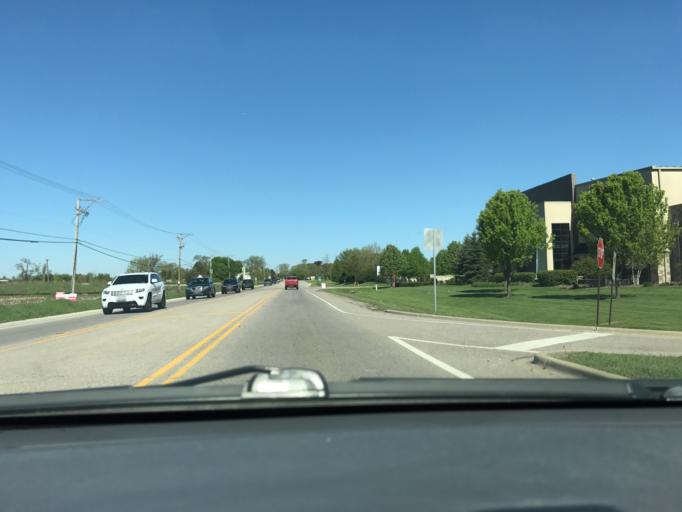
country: US
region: Illinois
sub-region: Kane County
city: Pingree Grove
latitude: 42.0398
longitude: -88.3649
